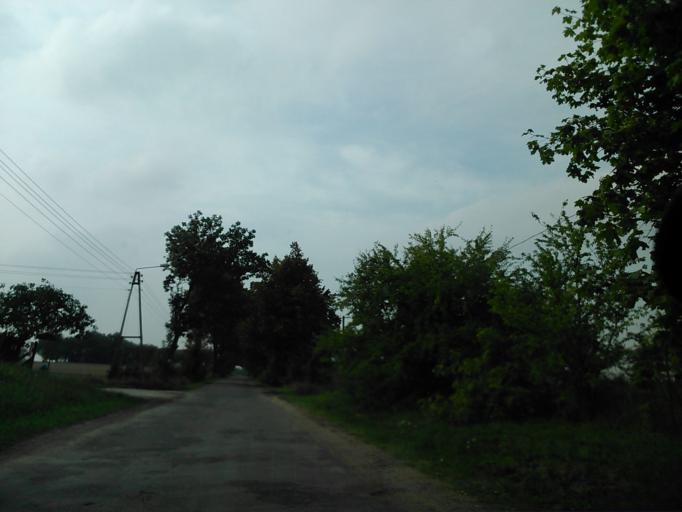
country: PL
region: Kujawsko-Pomorskie
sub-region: Powiat wabrzeski
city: Pluznica
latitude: 53.2357
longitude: 18.8211
